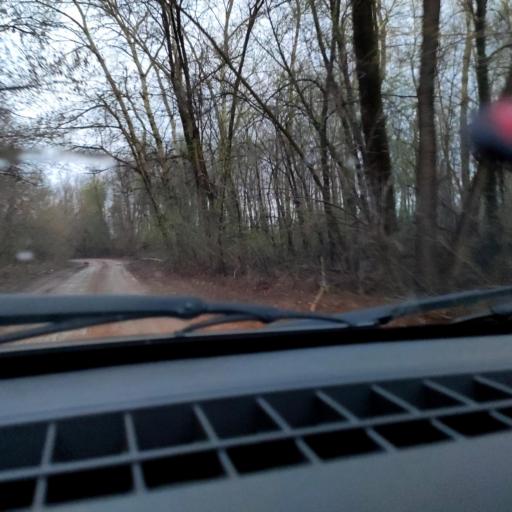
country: RU
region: Bashkortostan
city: Ufa
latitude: 54.6733
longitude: 55.9544
